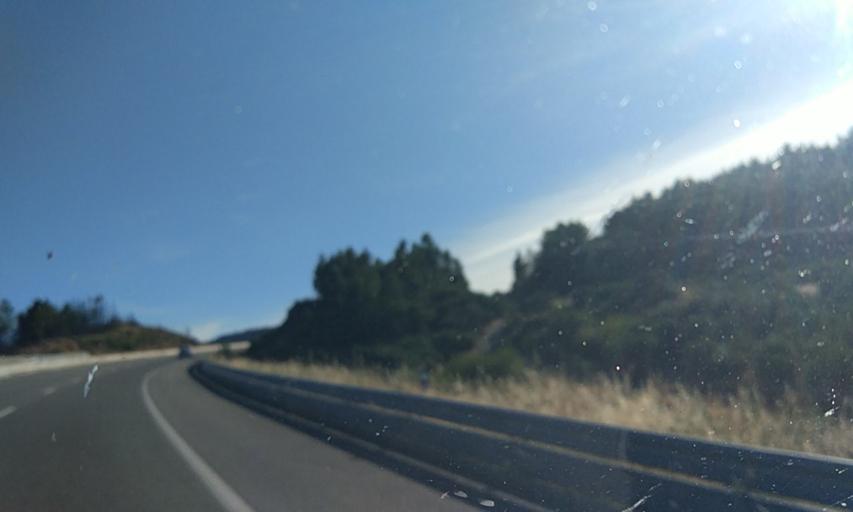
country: PT
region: Vila Real
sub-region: Murca
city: Murca
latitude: 41.3929
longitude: -7.4833
